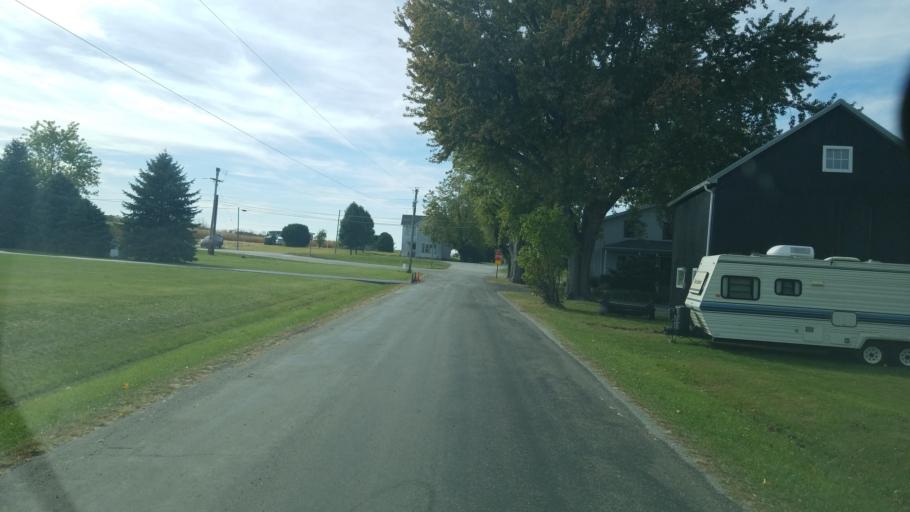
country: US
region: Ohio
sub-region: Highland County
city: Leesburg
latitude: 39.3247
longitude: -83.5841
